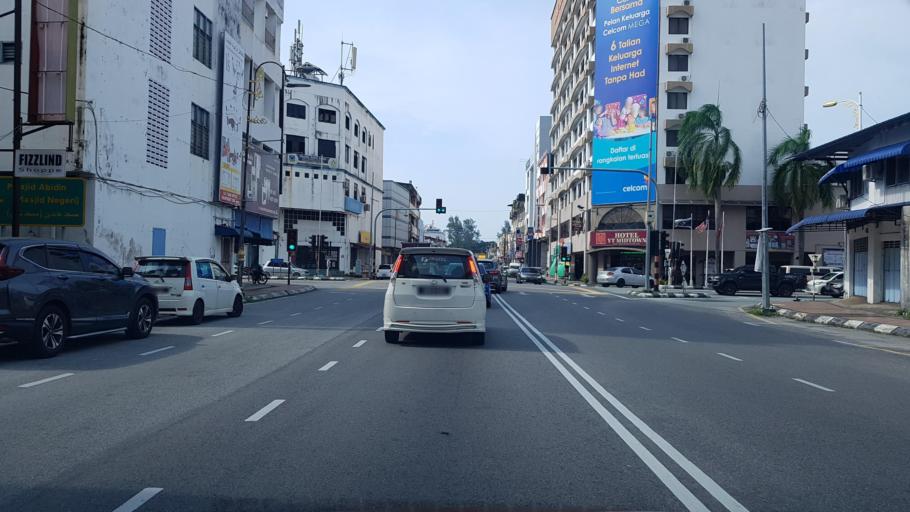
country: MY
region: Terengganu
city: Kuala Terengganu
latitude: 5.3335
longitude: 103.1388
